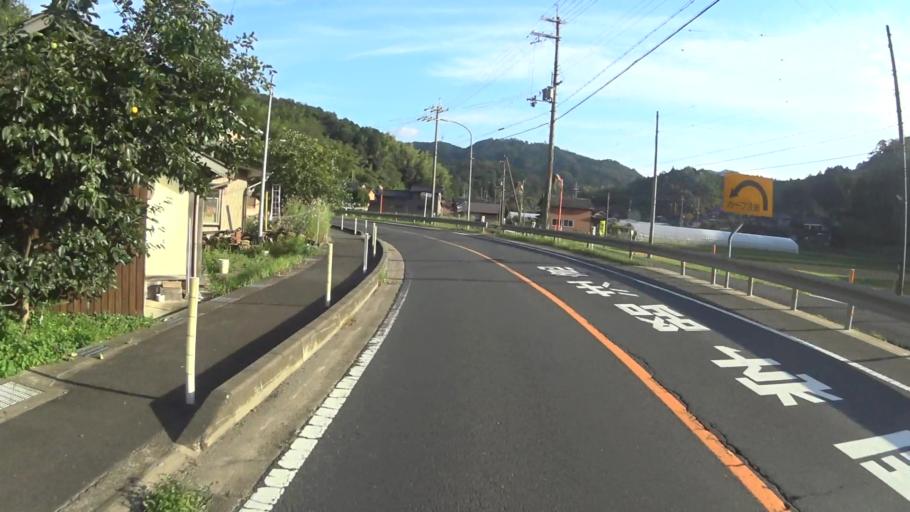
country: JP
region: Hyogo
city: Toyooka
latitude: 35.5948
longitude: 134.9057
